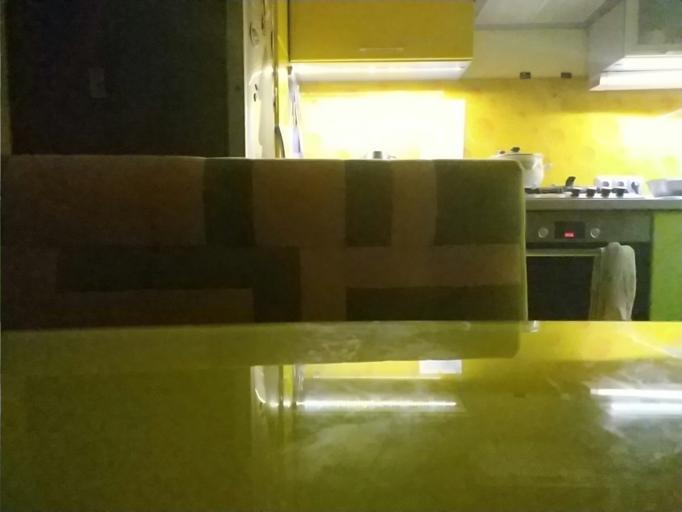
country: RU
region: Republic of Karelia
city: Pyaozerskiy
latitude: 65.5560
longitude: 30.5845
